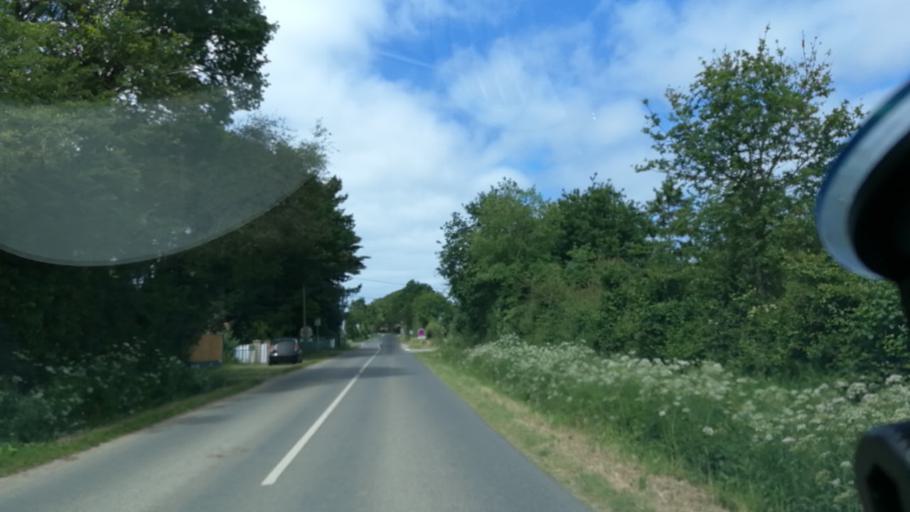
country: FR
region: Pays de la Loire
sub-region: Departement de la Loire-Atlantique
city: Asserac
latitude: 47.4395
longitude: -2.4303
